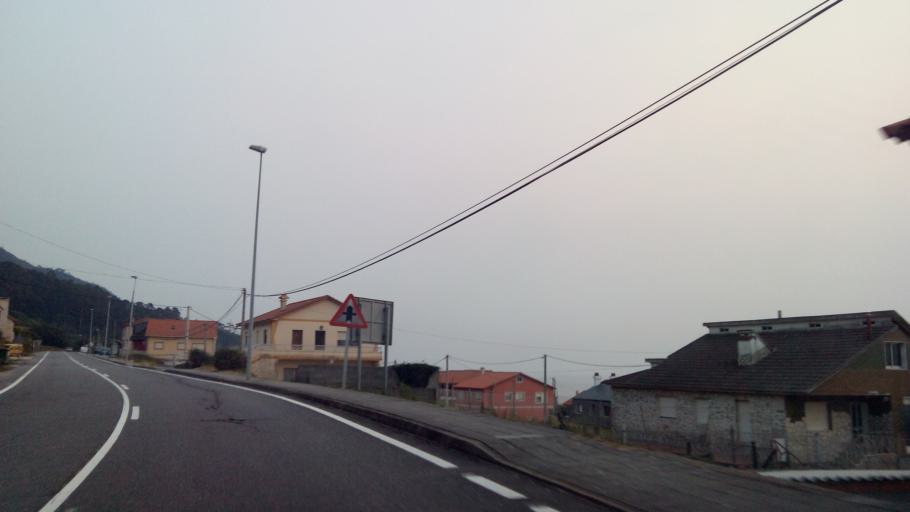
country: ES
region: Galicia
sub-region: Provincia de Pontevedra
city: Oia
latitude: 42.0000
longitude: -8.8757
